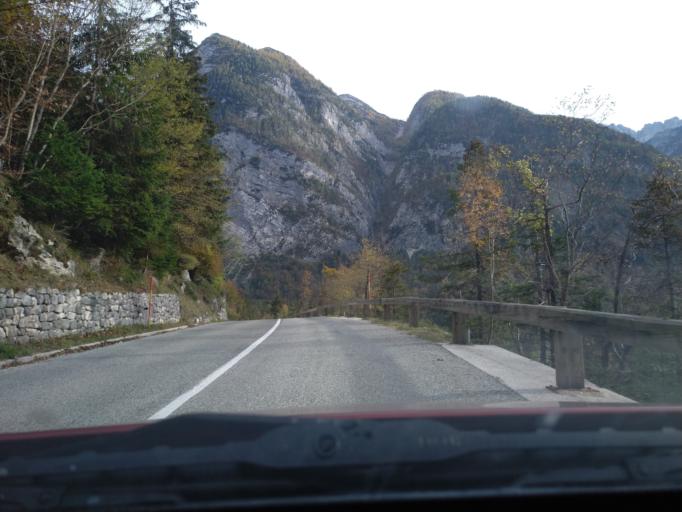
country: SI
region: Kranjska Gora
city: Kranjska Gora
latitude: 46.3859
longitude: 13.7510
